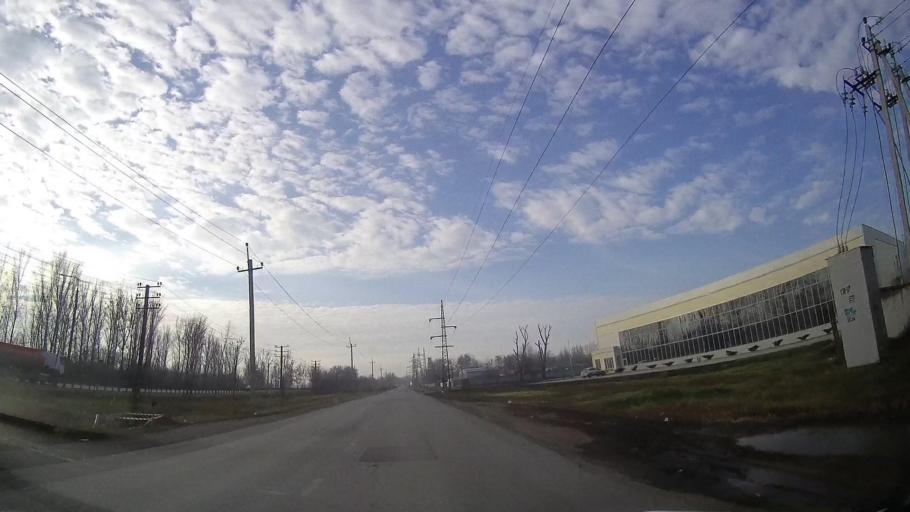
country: RU
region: Rostov
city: Bataysk
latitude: 47.1123
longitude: 39.7662
